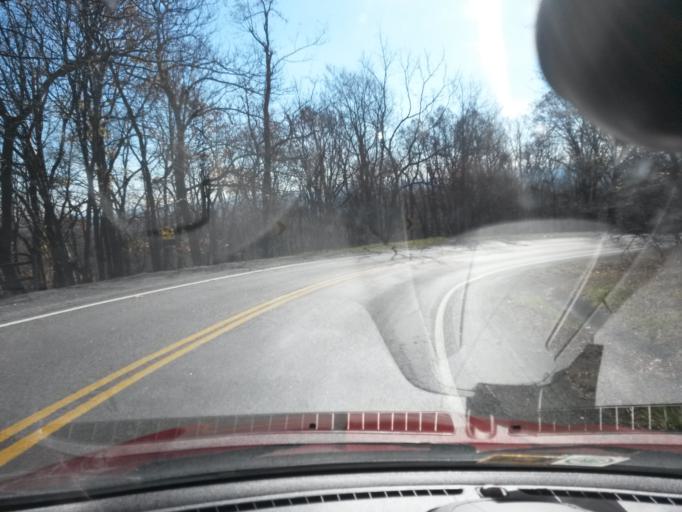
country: US
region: Virginia
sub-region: City of Bedford
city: Bedford
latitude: 37.4336
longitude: -79.5746
